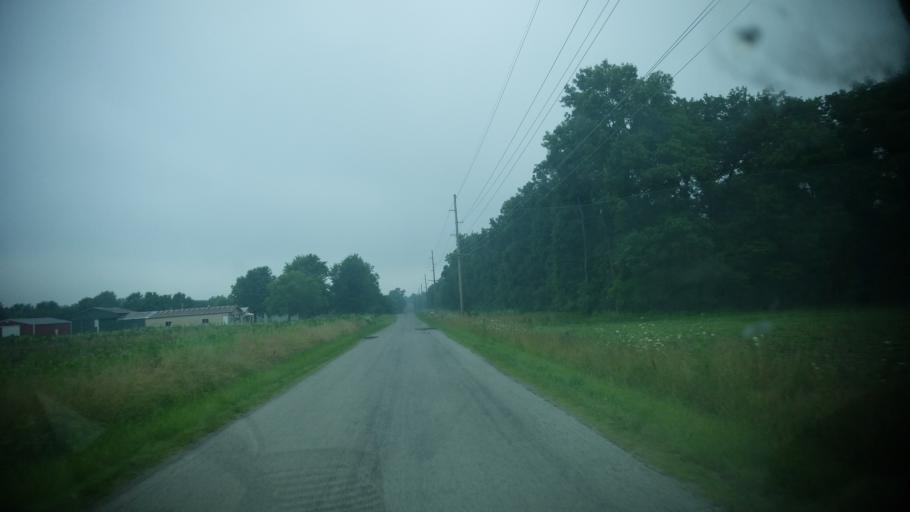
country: US
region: Illinois
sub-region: Clay County
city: Flora
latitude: 38.5544
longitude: -88.4019
